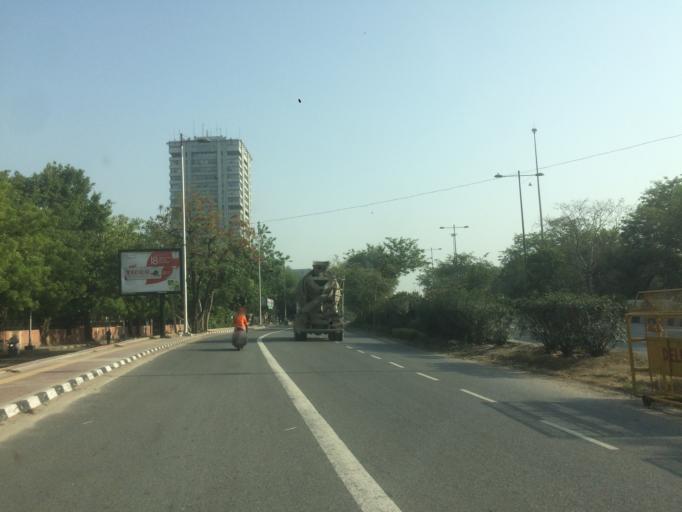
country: IN
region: NCT
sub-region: New Delhi
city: New Delhi
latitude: 28.6254
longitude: 77.2468
